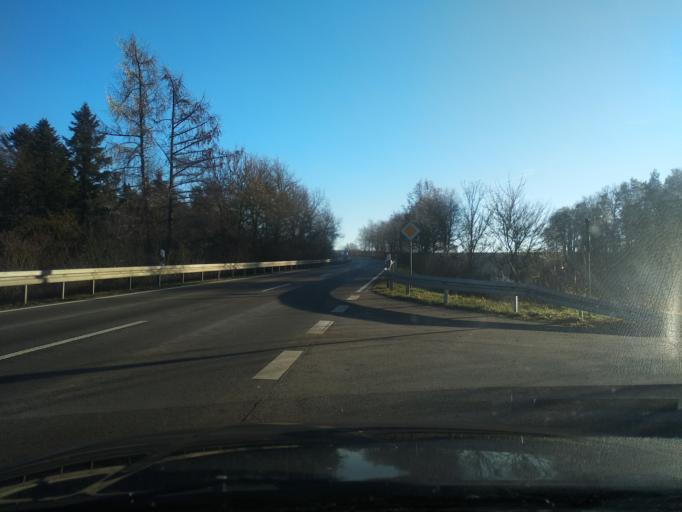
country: DE
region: Baden-Wuerttemberg
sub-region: Regierungsbezirk Stuttgart
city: Deckenpfronn
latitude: 48.6634
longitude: 8.8020
